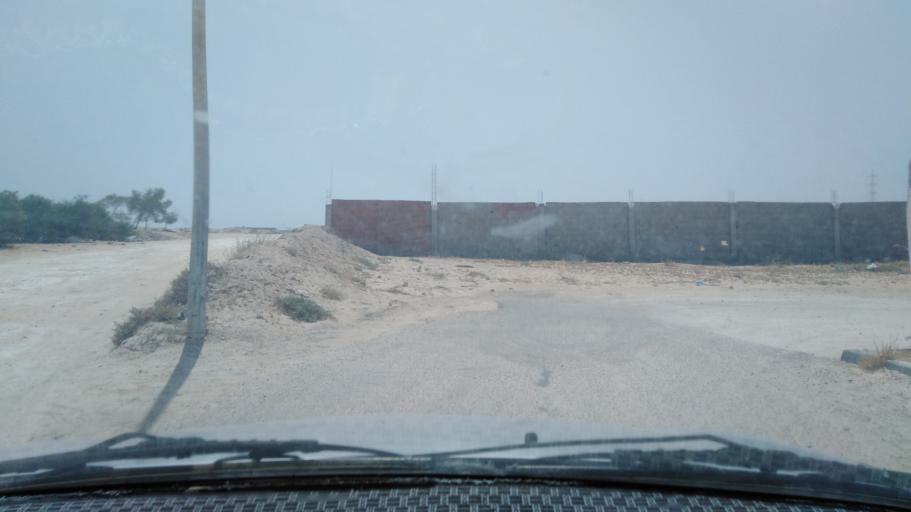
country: TN
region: Qabis
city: Gabes
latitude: 33.9514
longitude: 9.9973
